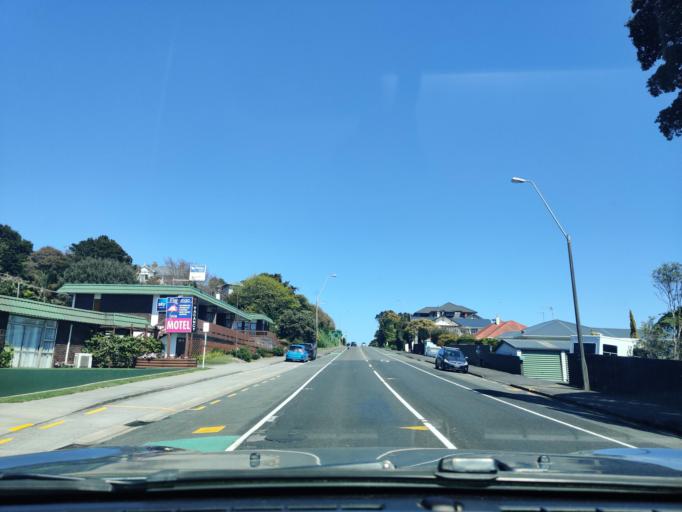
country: NZ
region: Taranaki
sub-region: New Plymouth District
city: New Plymouth
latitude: -39.0627
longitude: 174.0579
